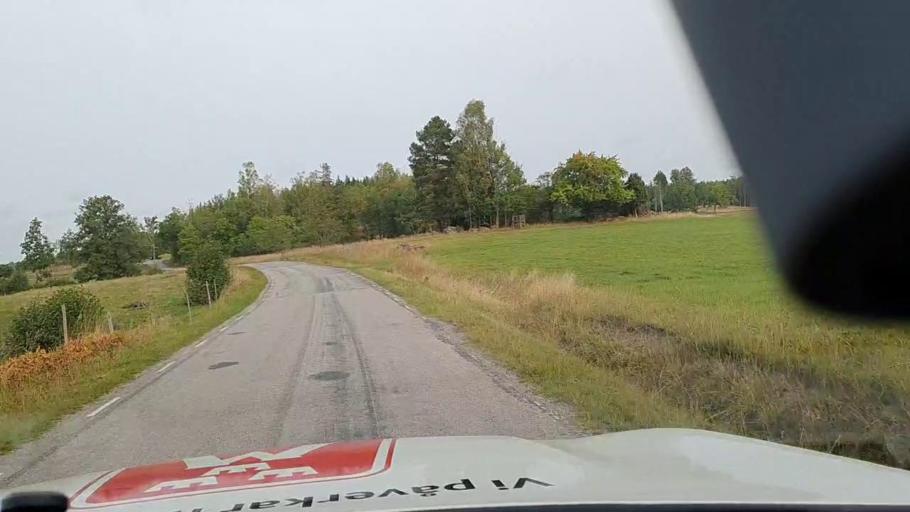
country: SE
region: Soedermanland
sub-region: Nykopings Kommun
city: Stigtomta
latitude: 58.9707
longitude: 16.9010
